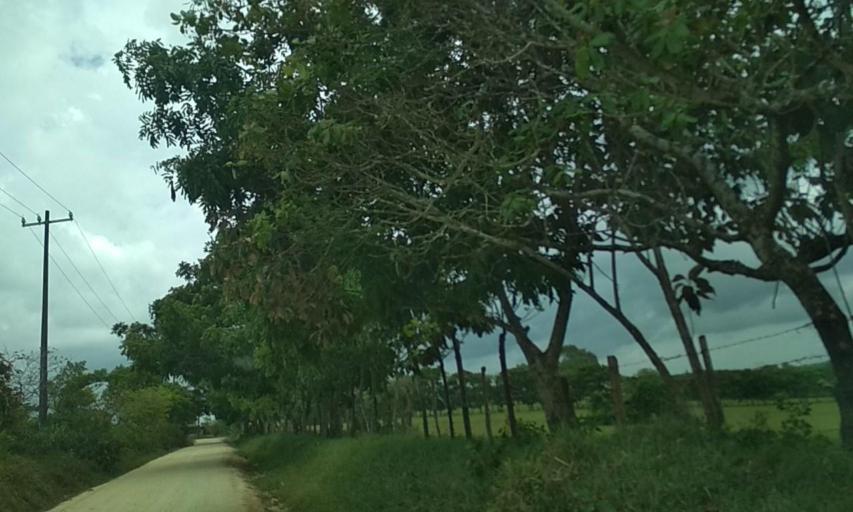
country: MX
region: Veracruz
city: Las Choapas
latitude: 17.8909
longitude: -94.1159
